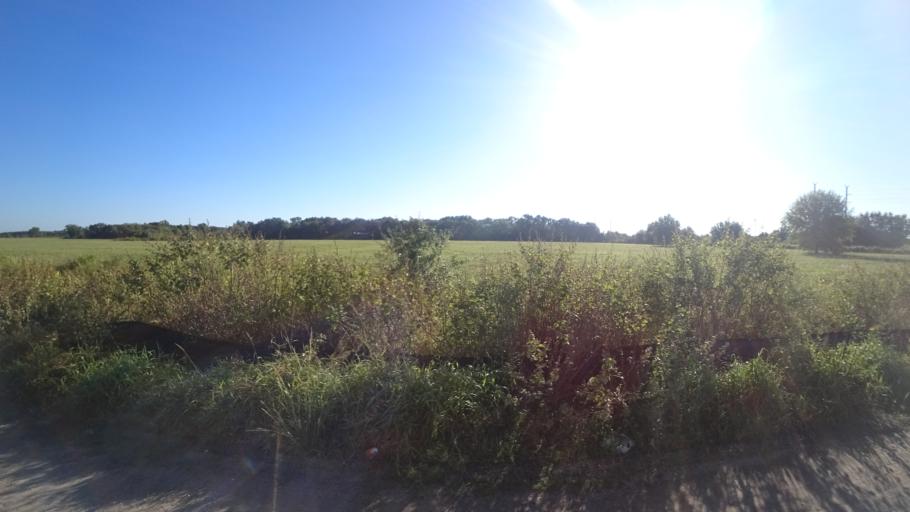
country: US
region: Florida
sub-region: Manatee County
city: Ellenton
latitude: 27.6243
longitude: -82.4880
